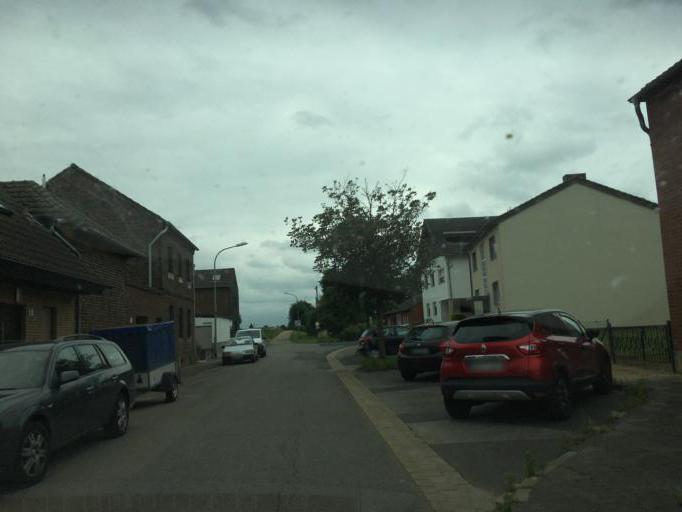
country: DE
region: North Rhine-Westphalia
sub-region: Regierungsbezirk Koln
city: Merzenich
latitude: 50.7842
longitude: 6.5488
